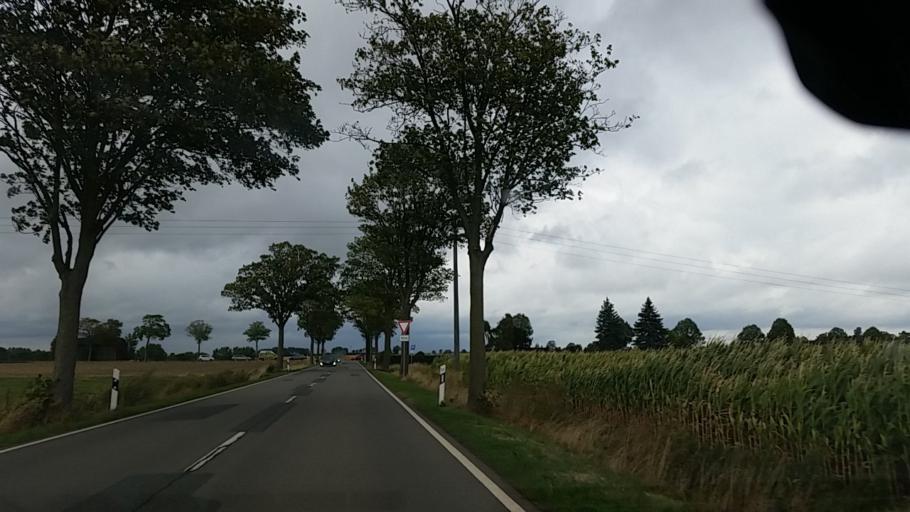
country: DE
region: Lower Saxony
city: Calberlah
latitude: 52.3929
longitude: 10.6444
